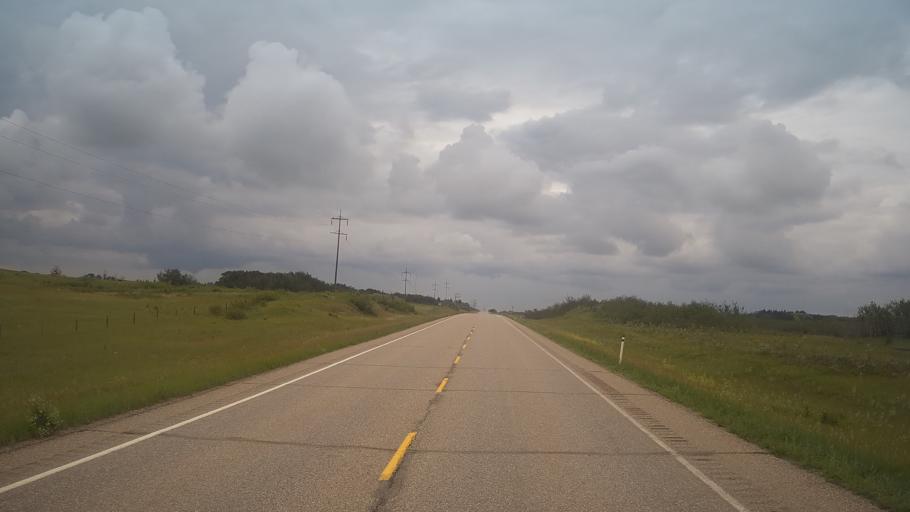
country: CA
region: Alberta
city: Wainwright
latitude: 52.5590
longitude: -111.0398
